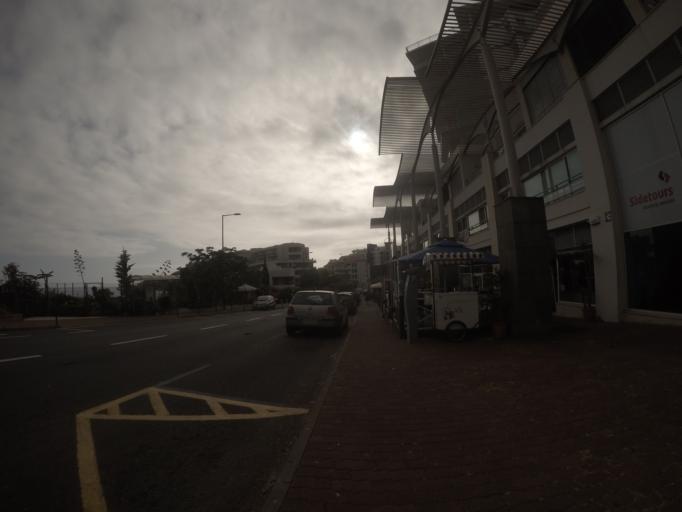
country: PT
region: Madeira
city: Camara de Lobos
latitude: 32.6348
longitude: -16.9434
